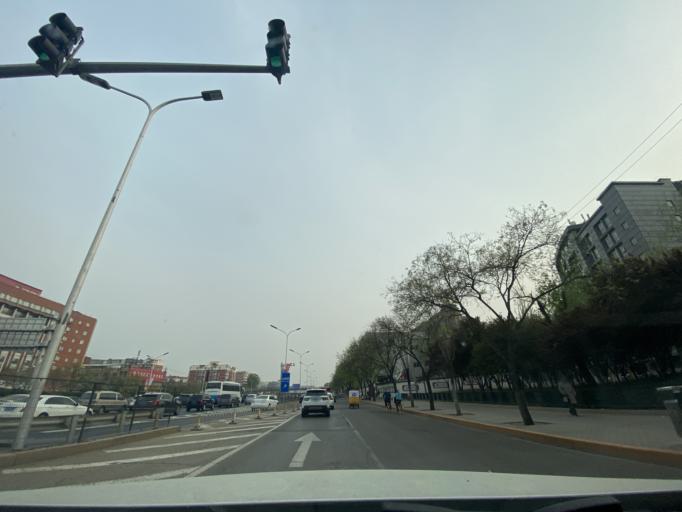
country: CN
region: Beijing
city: Sijiqing
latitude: 39.9374
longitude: 116.2679
